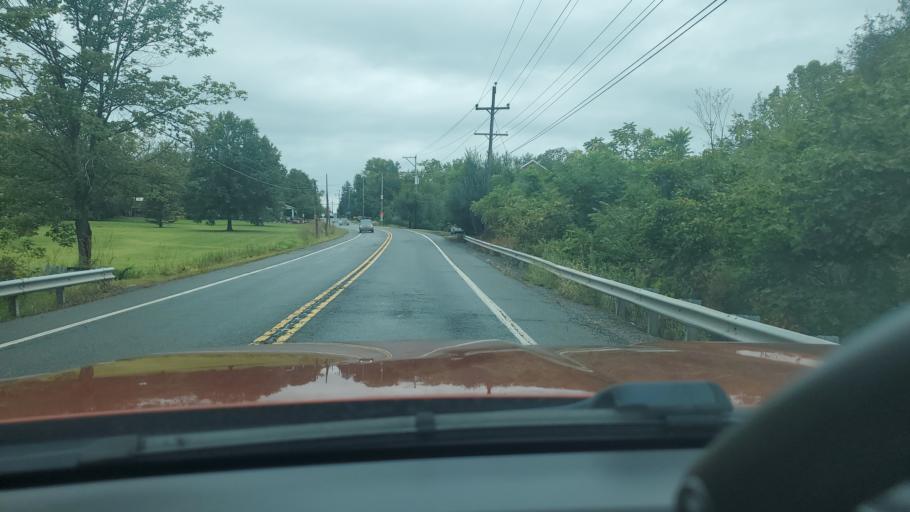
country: US
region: Pennsylvania
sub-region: Montgomery County
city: Woxall
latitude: 40.3027
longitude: -75.4801
